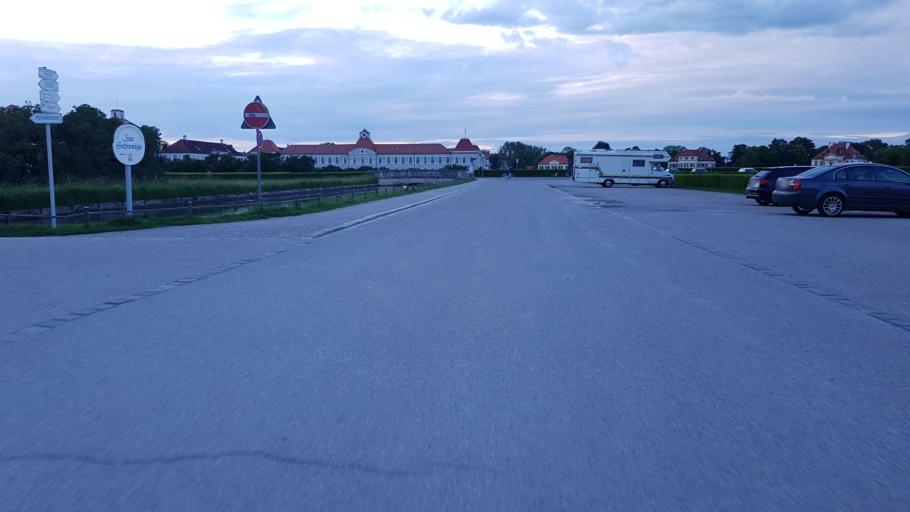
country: DE
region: Bavaria
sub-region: Upper Bavaria
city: Pasing
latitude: 48.1566
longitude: 11.5059
